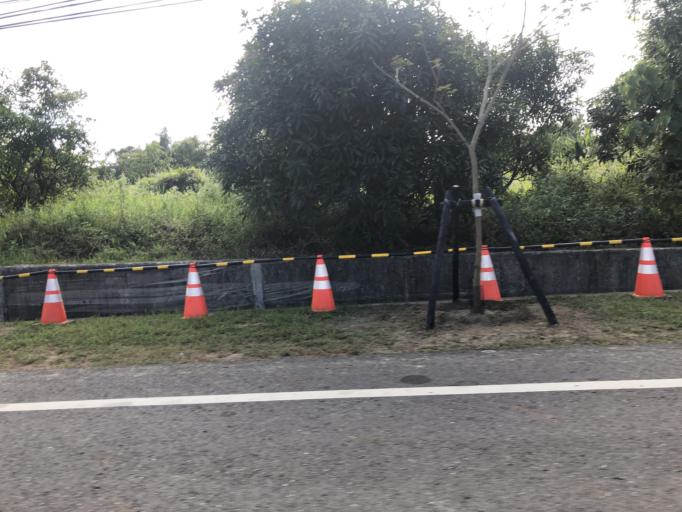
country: TW
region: Taiwan
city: Yujing
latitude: 23.0480
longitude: 120.4234
